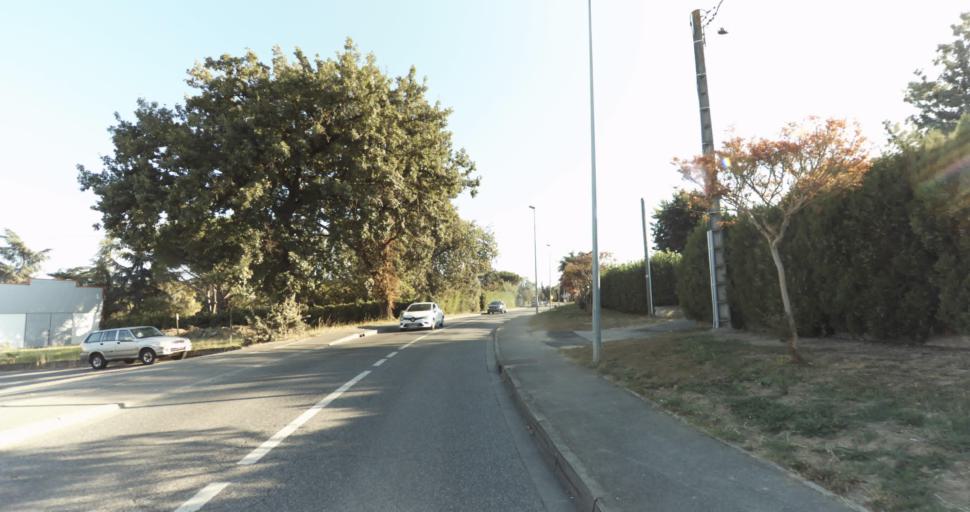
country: FR
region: Midi-Pyrenees
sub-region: Departement de la Haute-Garonne
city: L'Union
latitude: 43.6633
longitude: 1.4709
